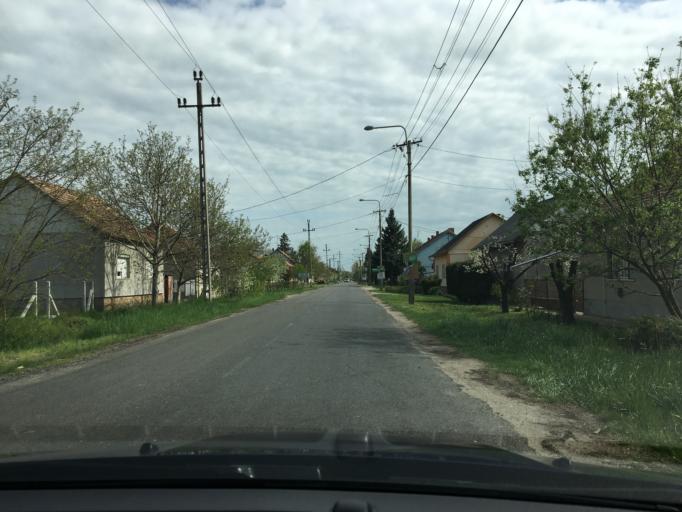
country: HU
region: Csongrad
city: Algyo
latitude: 46.3436
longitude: 20.2064
